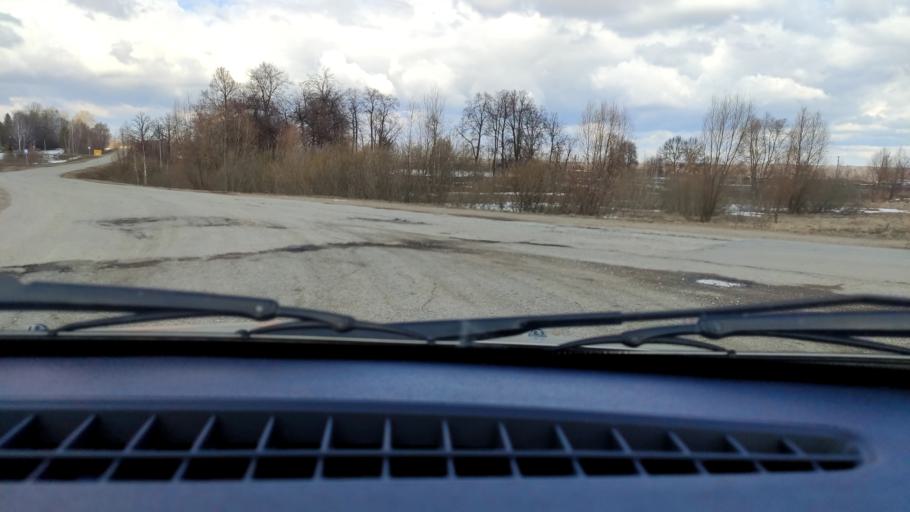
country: RU
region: Bashkortostan
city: Kudeyevskiy
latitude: 54.8510
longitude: 56.7954
